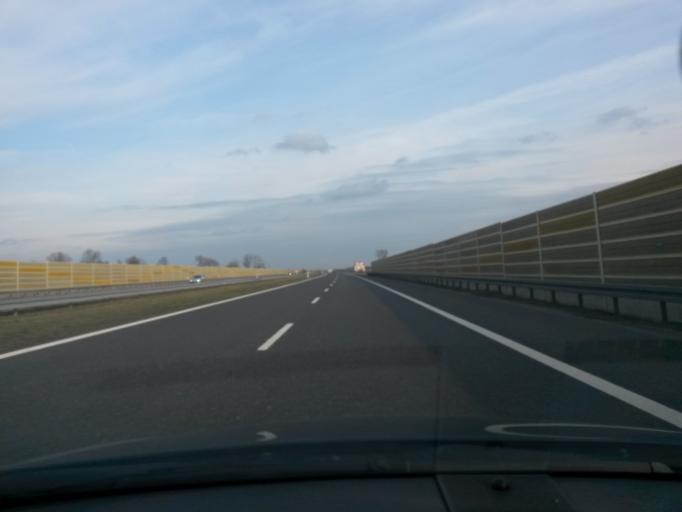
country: PL
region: Lodz Voivodeship
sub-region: Powiat poddebicki
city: Dalikow
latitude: 51.9708
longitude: 19.0926
